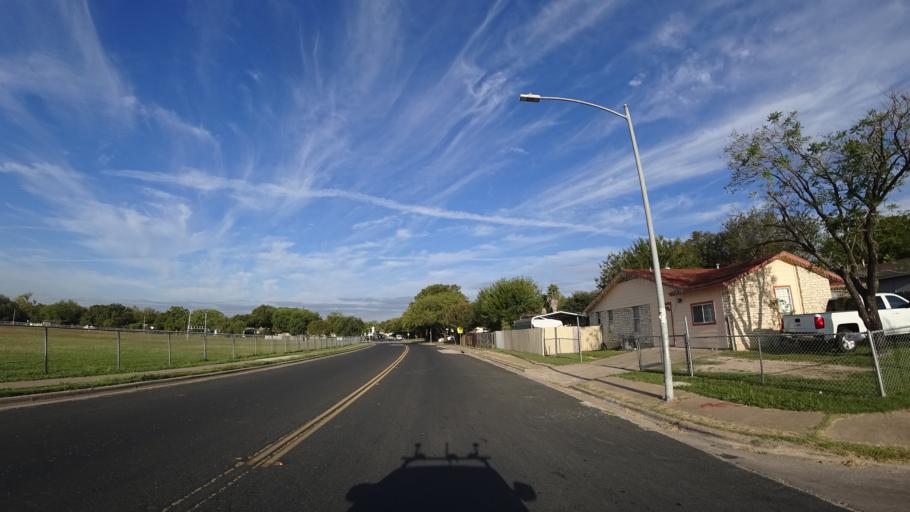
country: US
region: Texas
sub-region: Travis County
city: Onion Creek
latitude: 30.1906
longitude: -97.7434
